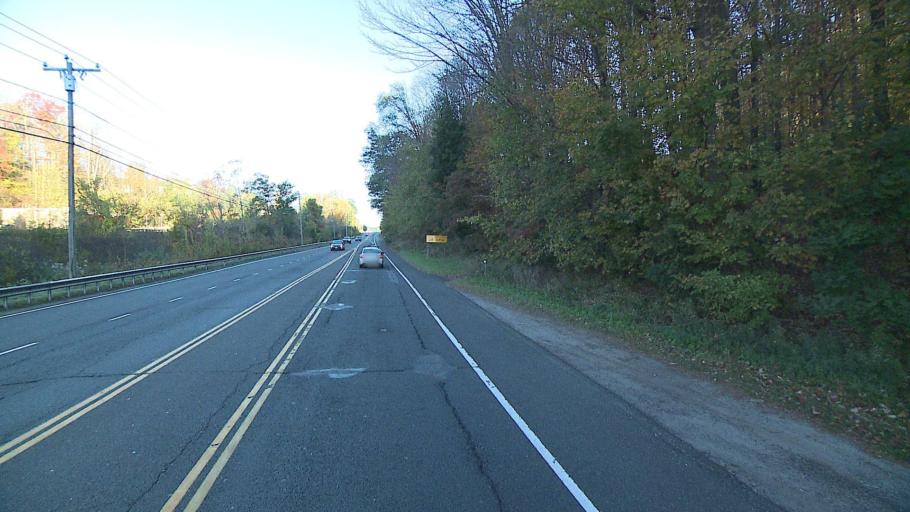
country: US
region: Connecticut
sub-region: Litchfield County
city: Winsted
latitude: 41.9105
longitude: -73.0494
